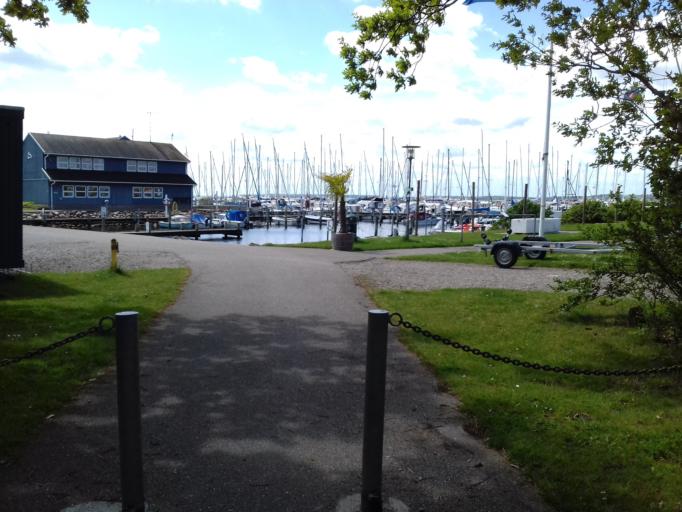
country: DK
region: South Denmark
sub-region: Sonderborg Kommune
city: Sonderborg
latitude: 54.8998
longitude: 9.7945
